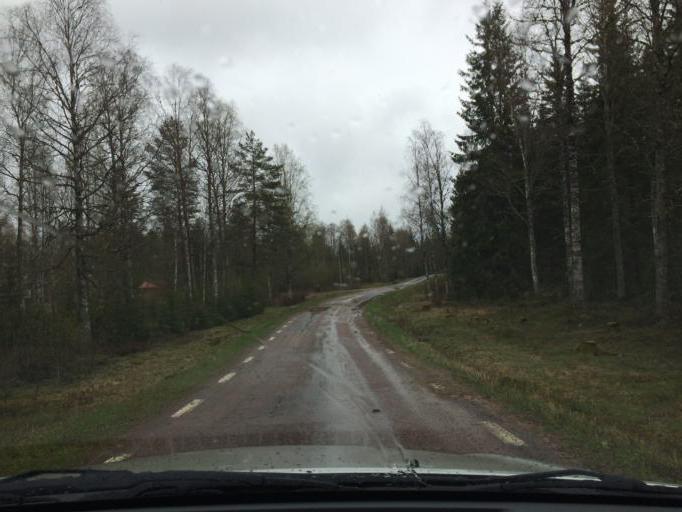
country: SE
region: OErebro
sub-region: Hallefors Kommun
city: Haellefors
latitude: 60.0395
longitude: 14.5259
